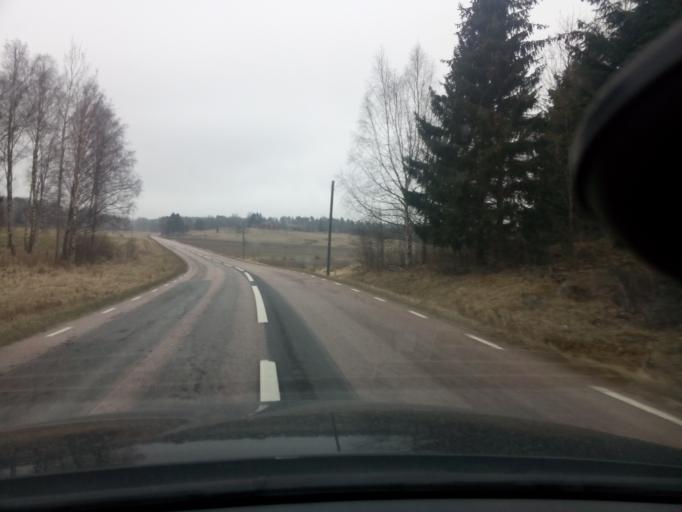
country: SE
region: Soedermanland
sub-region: Gnesta Kommun
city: Gnesta
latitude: 59.0218
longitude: 17.1693
